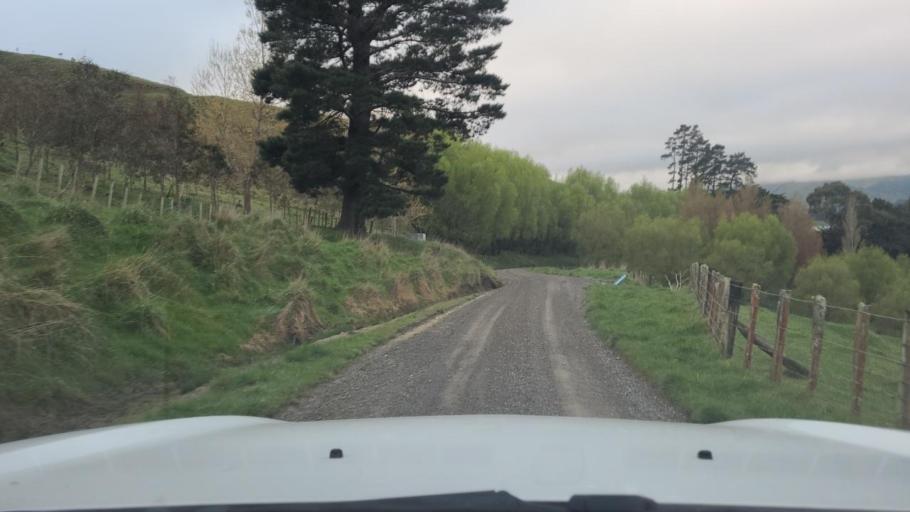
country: NZ
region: Wellington
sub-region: Masterton District
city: Masterton
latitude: -41.1598
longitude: 175.6801
